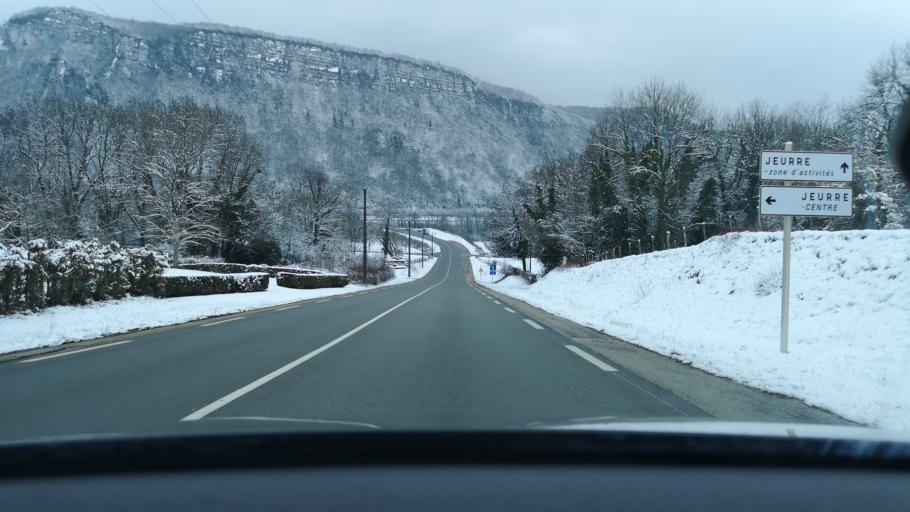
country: FR
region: Rhone-Alpes
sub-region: Departement de l'Ain
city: Dortan
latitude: 46.3681
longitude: 5.7043
